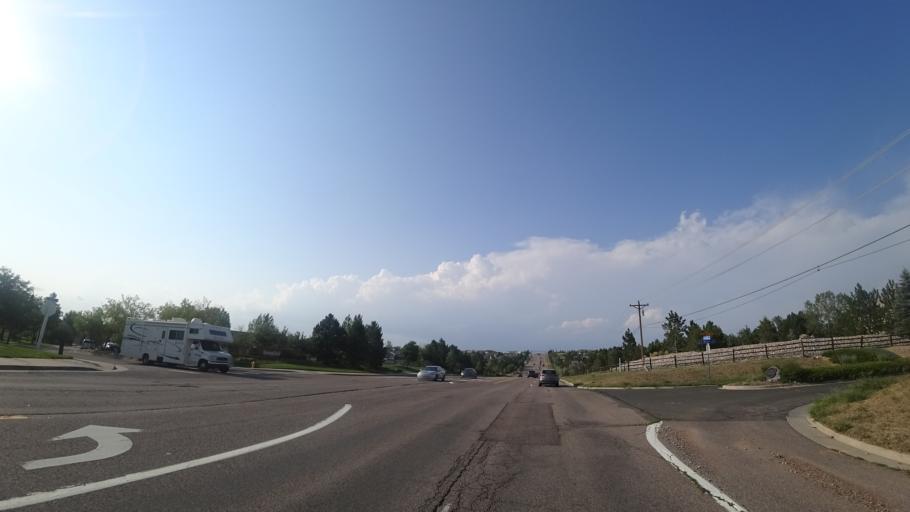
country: US
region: Colorado
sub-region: Douglas County
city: Parker
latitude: 39.6001
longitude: -104.7448
